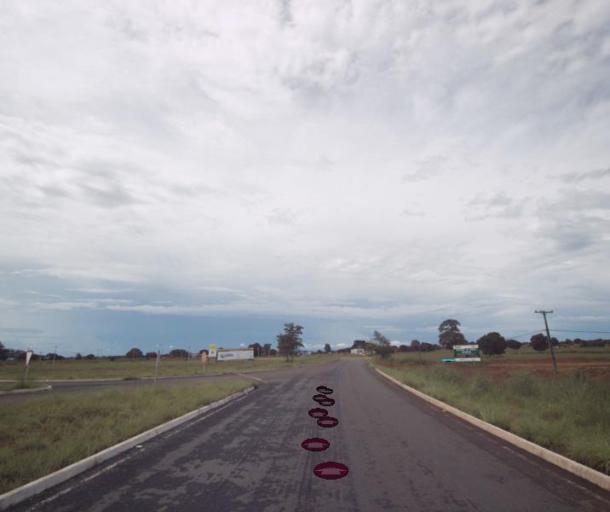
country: BR
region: Goias
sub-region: Sao Miguel Do Araguaia
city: Sao Miguel do Araguaia
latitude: -13.2852
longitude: -50.1839
